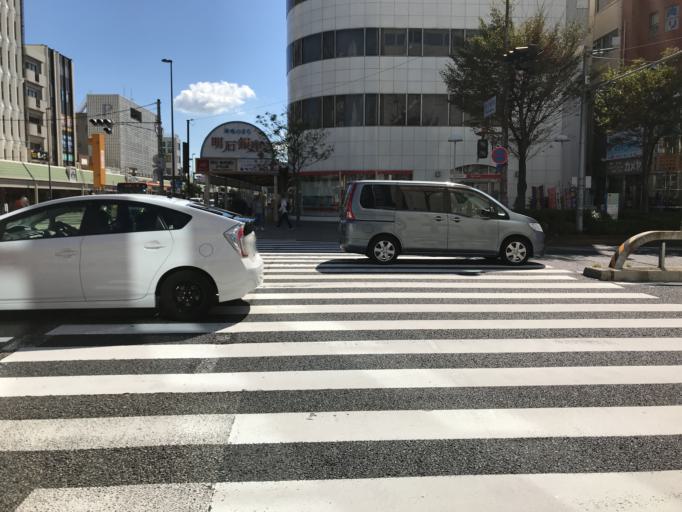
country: JP
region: Hyogo
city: Akashi
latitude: 34.6476
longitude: 134.9934
